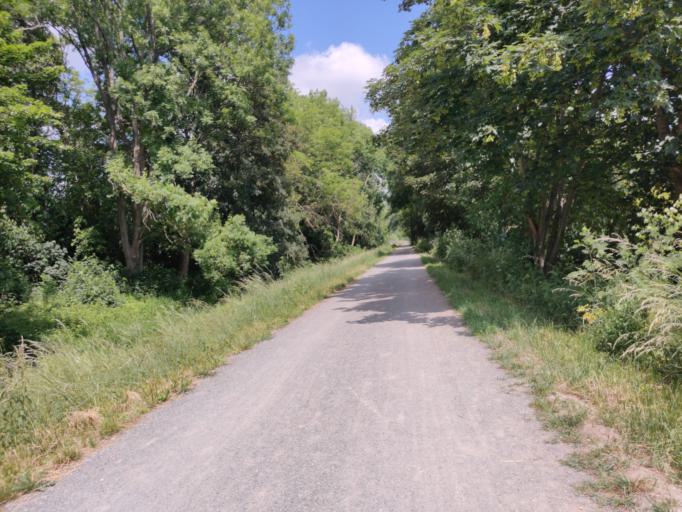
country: DE
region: Lower Saxony
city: Hildesheim
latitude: 52.1642
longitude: 9.9221
